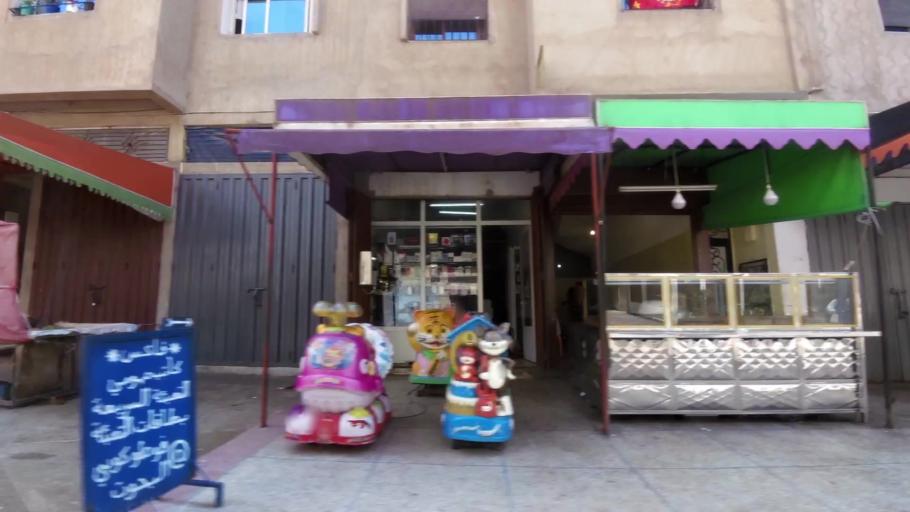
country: MA
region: Grand Casablanca
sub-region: Nouaceur
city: Dar Bouazza
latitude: 33.5309
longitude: -7.7348
